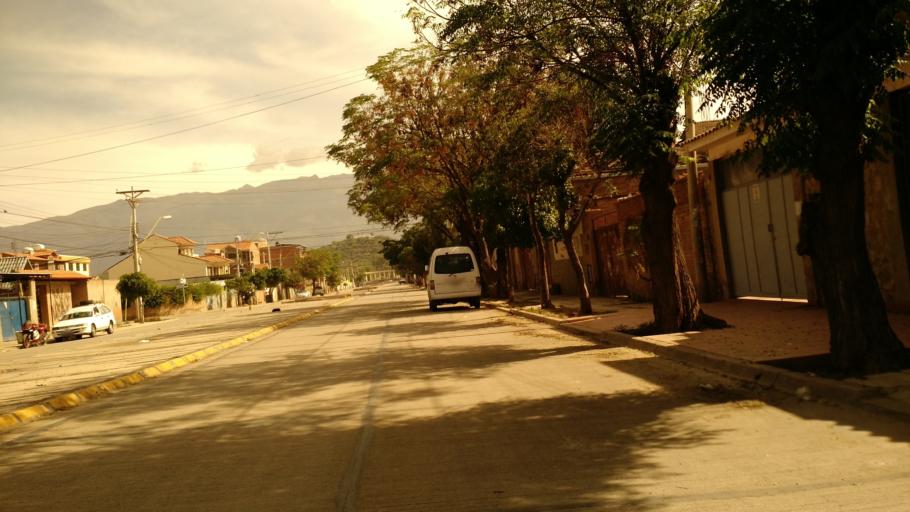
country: BO
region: Cochabamba
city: Cochabamba
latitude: -17.4169
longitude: -66.1593
